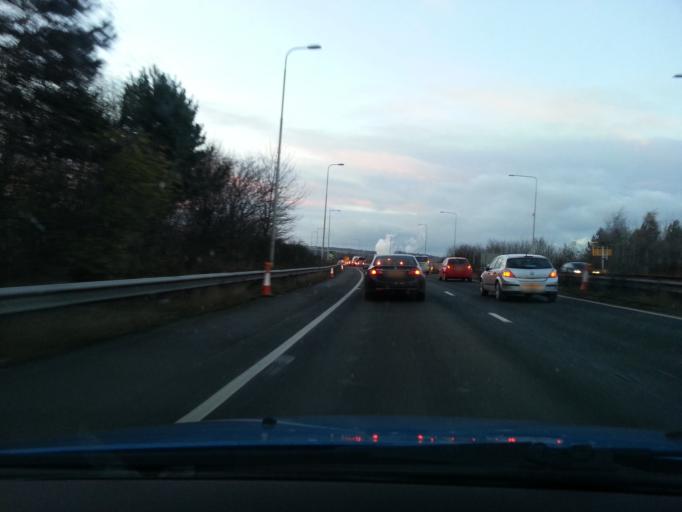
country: GB
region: England
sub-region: Gateshead
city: Lamesley
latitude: 54.9196
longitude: -1.6018
